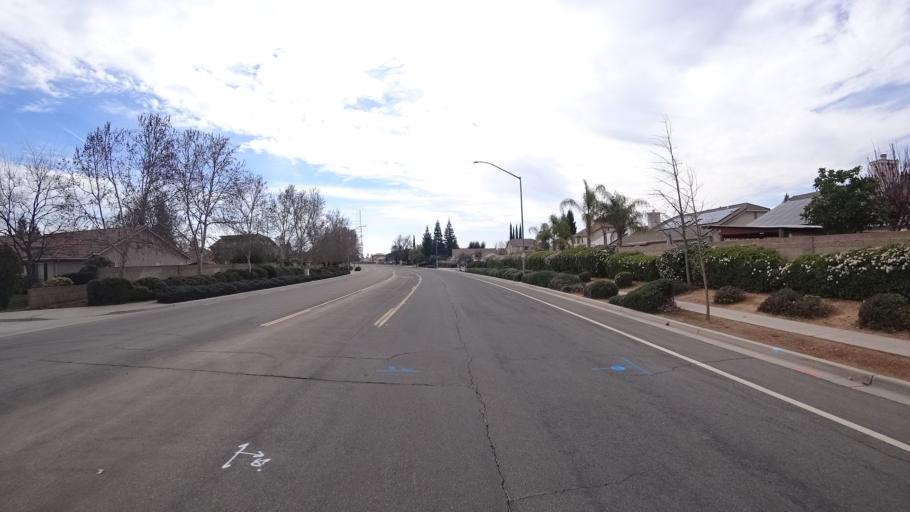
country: US
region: California
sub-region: Fresno County
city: West Park
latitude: 36.8203
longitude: -119.8840
